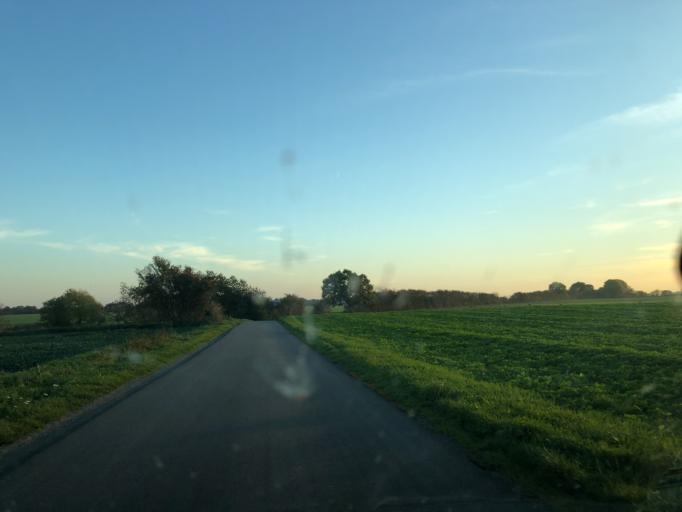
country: DK
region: South Denmark
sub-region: Vejle Kommune
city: Borkop
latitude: 55.6203
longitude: 9.6484
